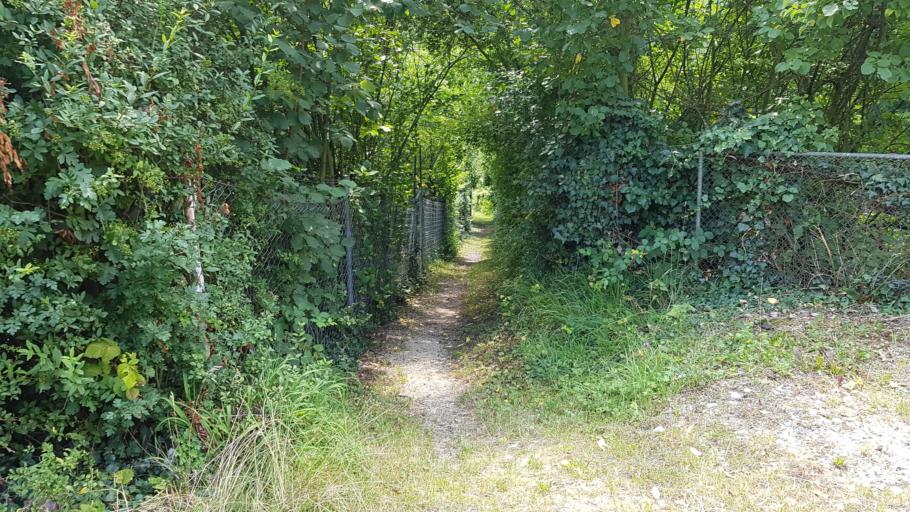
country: DE
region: Baden-Wuerttemberg
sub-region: Regierungsbezirk Stuttgart
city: Stuttgart Muehlhausen
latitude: 48.8275
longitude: 9.2033
